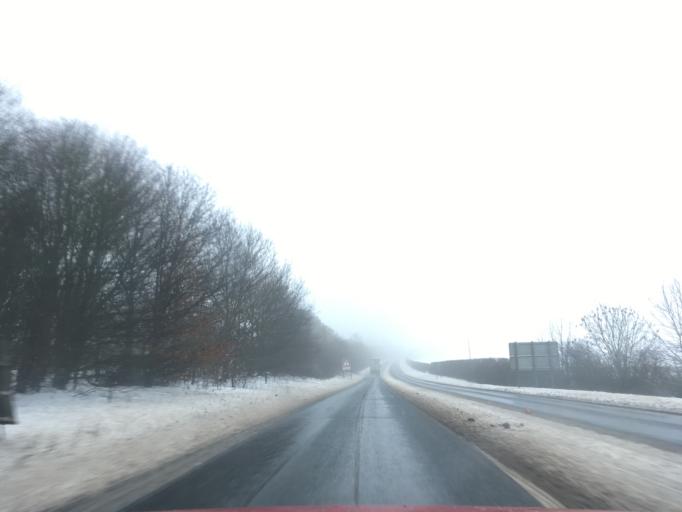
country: GB
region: England
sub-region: Warwickshire
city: Stratford-upon-Avon
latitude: 52.2337
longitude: -1.6775
